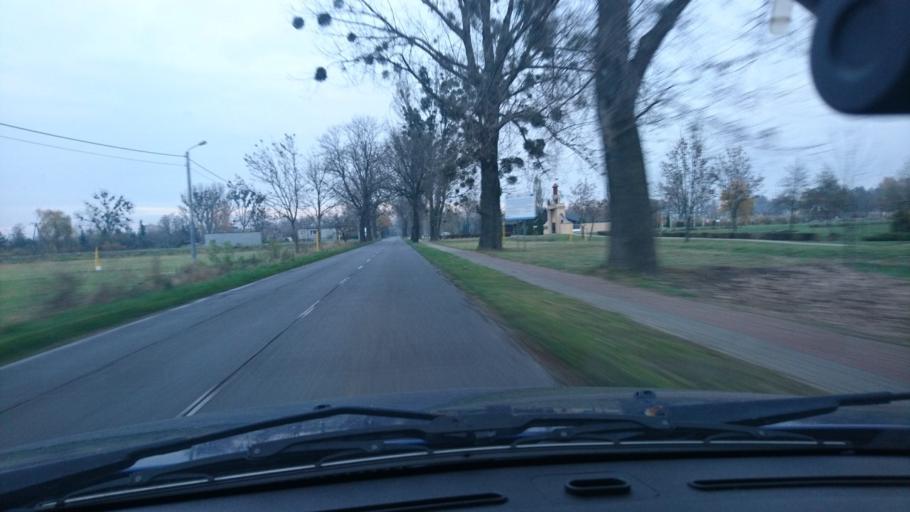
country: PL
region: Greater Poland Voivodeship
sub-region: Powiat ostrowski
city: Odolanow
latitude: 51.5699
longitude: 17.6660
